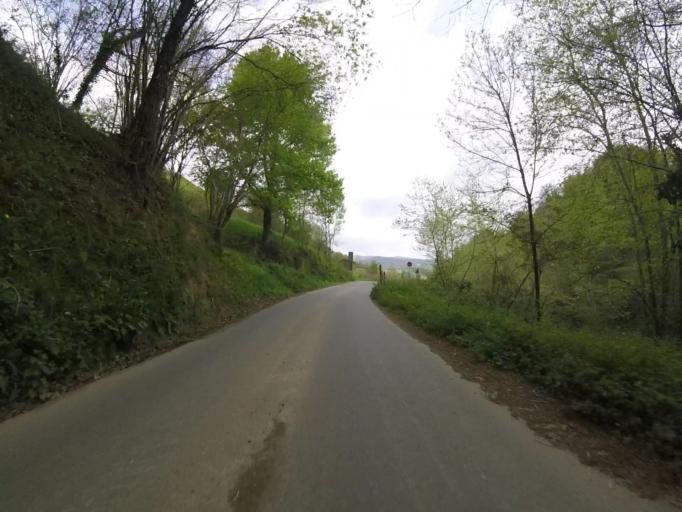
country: ES
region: Basque Country
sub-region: Provincia de Guipuzcoa
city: Zizurkil
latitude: 43.1834
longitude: -2.0830
